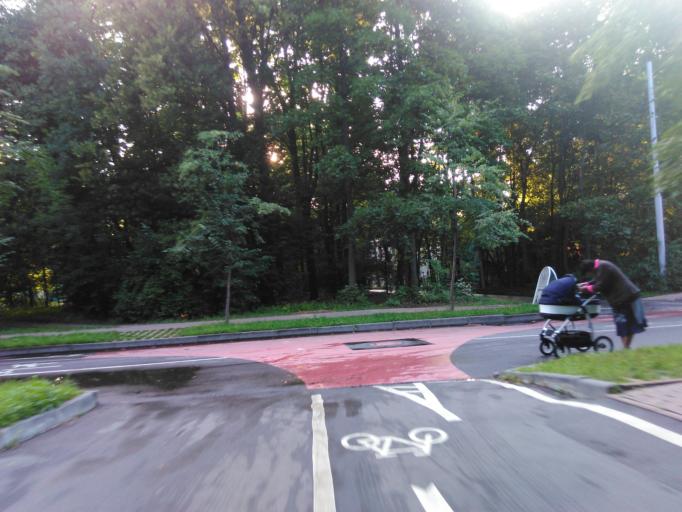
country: RU
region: Moscow
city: Sokol'niki
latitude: 55.7937
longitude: 37.6666
